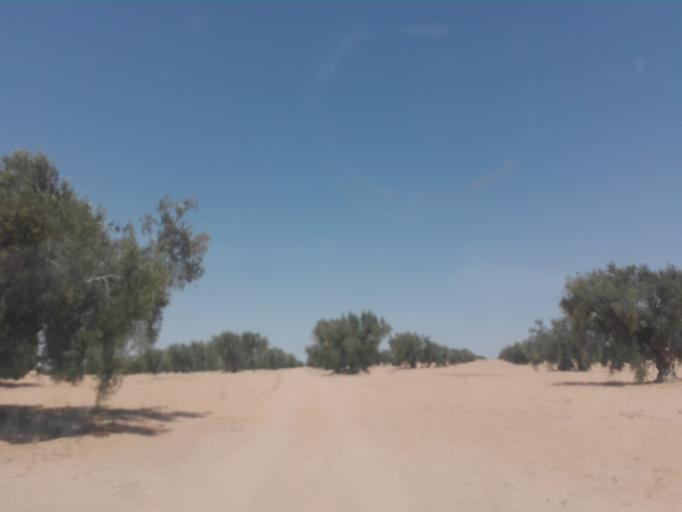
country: TN
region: Safaqis
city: Bi'r `Ali Bin Khalifah
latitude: 34.6491
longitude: 10.2698
